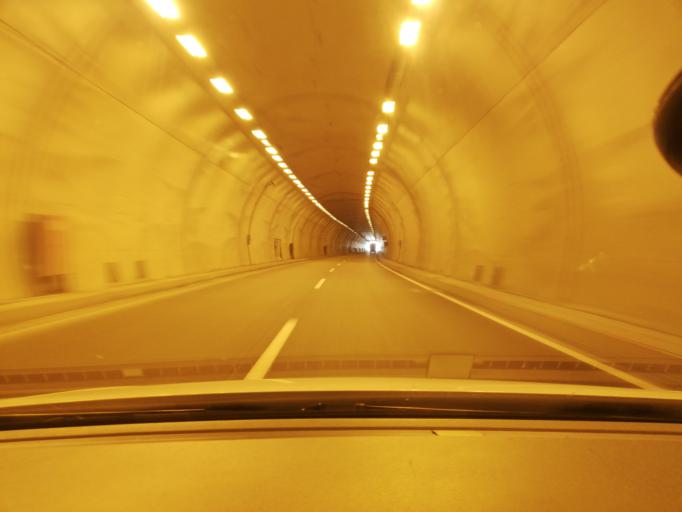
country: TR
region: Zonguldak
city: Alapli
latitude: 41.1654
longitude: 31.3629
